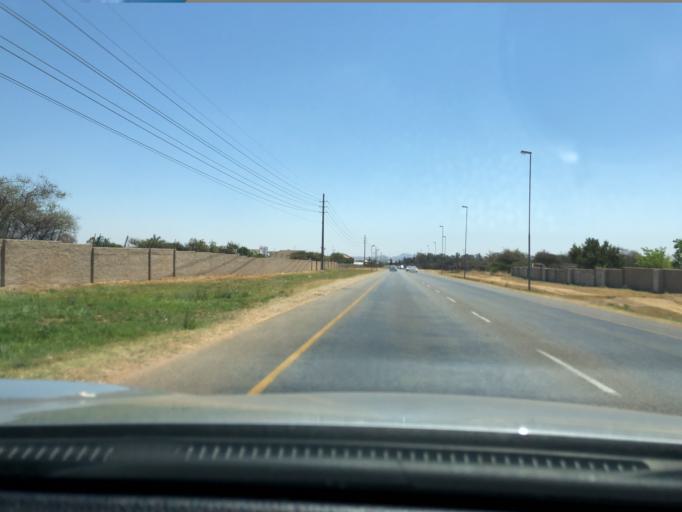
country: ZA
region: Limpopo
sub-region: Capricorn District Municipality
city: Polokwane
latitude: -23.8761
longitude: 29.4912
